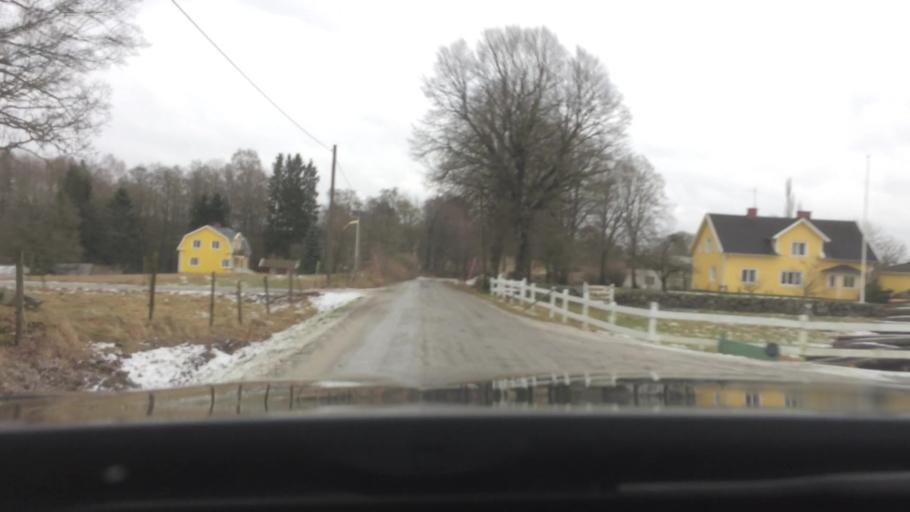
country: SE
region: Vaestra Goetaland
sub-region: Falkopings Kommun
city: Floby
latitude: 57.9978
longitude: 13.3914
